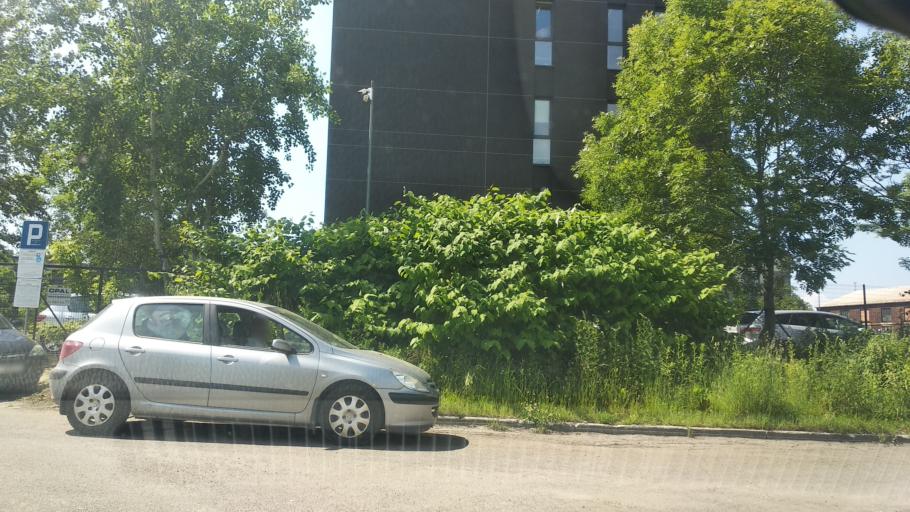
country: PL
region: Silesian Voivodeship
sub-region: Katowice
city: Katowice
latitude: 50.2661
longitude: 19.0001
